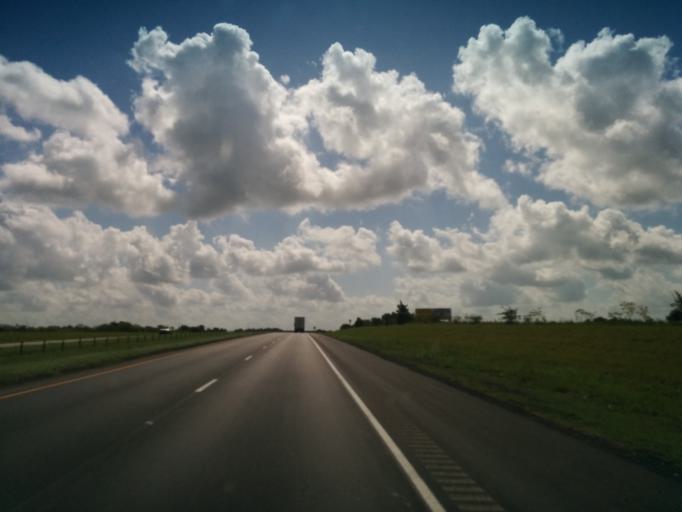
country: US
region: Texas
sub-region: Colorado County
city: Weimar
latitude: 29.6889
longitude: -96.8150
